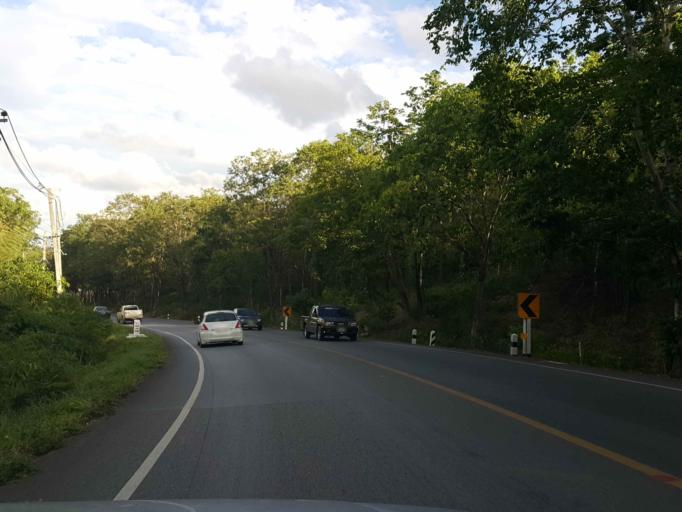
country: TH
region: Tak
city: Tak
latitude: 16.8072
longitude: 98.9949
